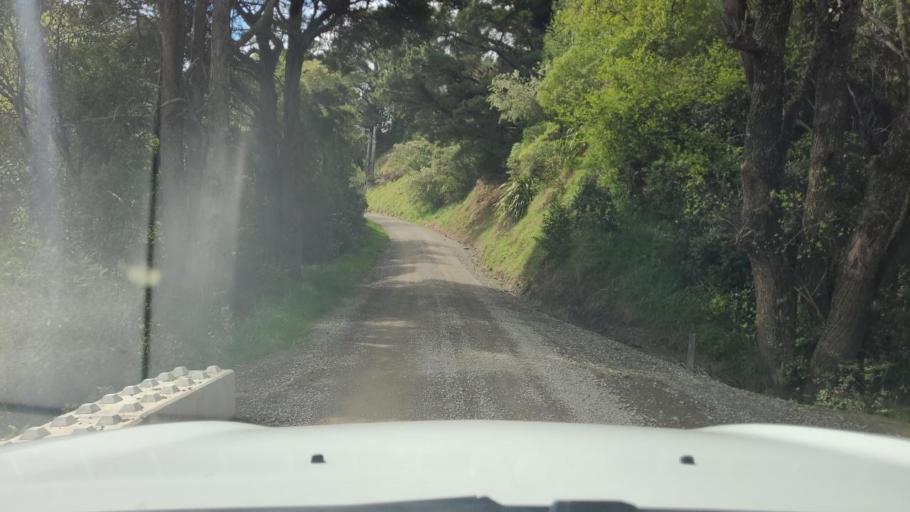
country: NZ
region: Wellington
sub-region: South Wairarapa District
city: Waipawa
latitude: -41.2150
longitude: 175.5882
